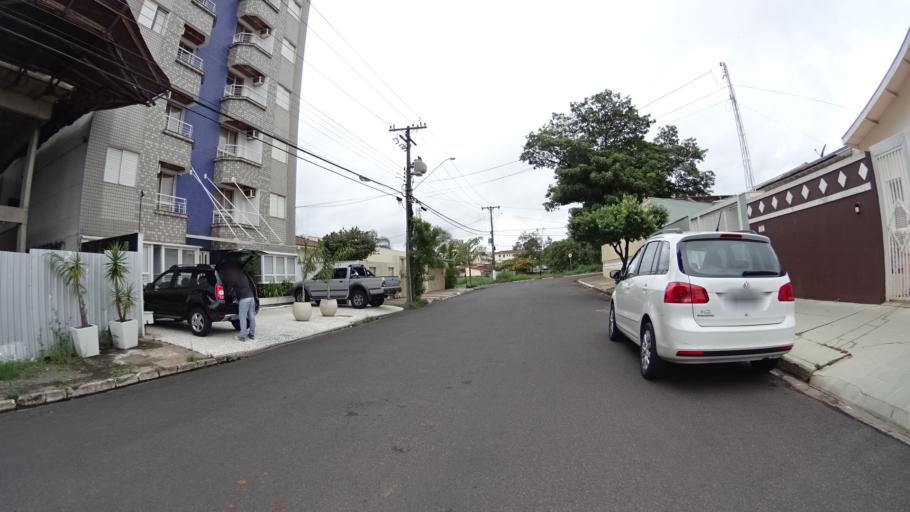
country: BR
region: Sao Paulo
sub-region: Marilia
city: Marilia
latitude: -22.2291
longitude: -49.9375
